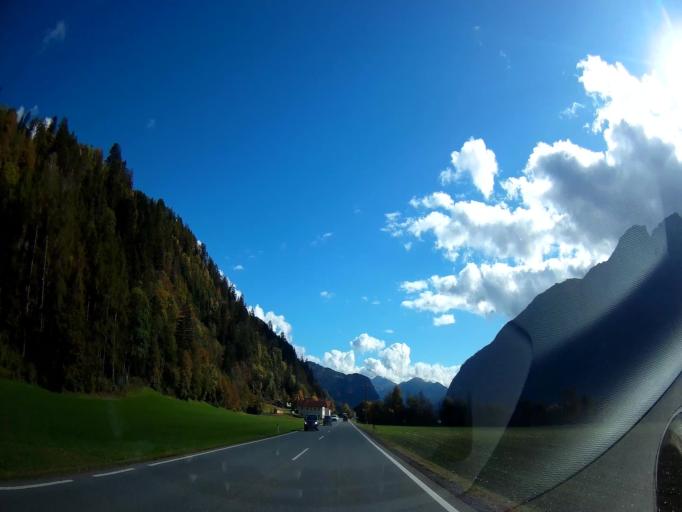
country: AT
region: Tyrol
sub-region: Politischer Bezirk Lienz
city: Lavant
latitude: 46.8100
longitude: 12.8517
